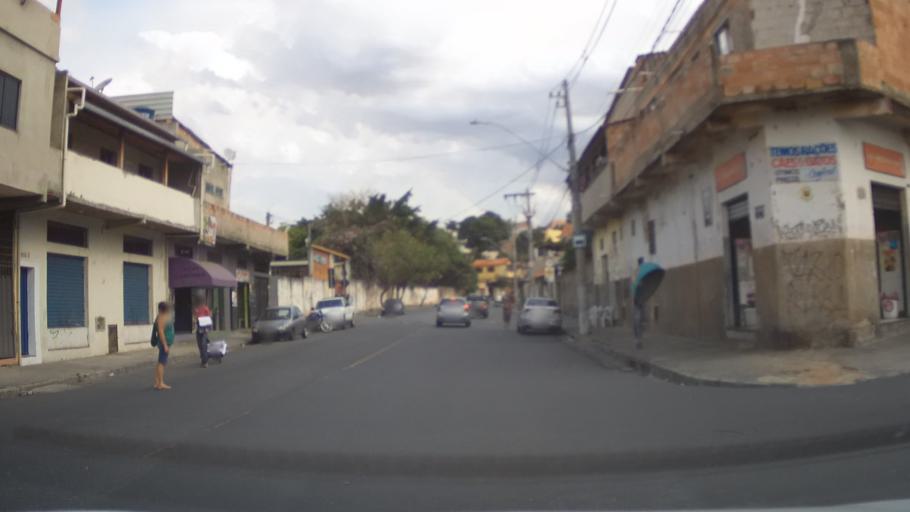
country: BR
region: Minas Gerais
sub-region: Belo Horizonte
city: Belo Horizonte
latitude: -19.8582
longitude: -43.8975
